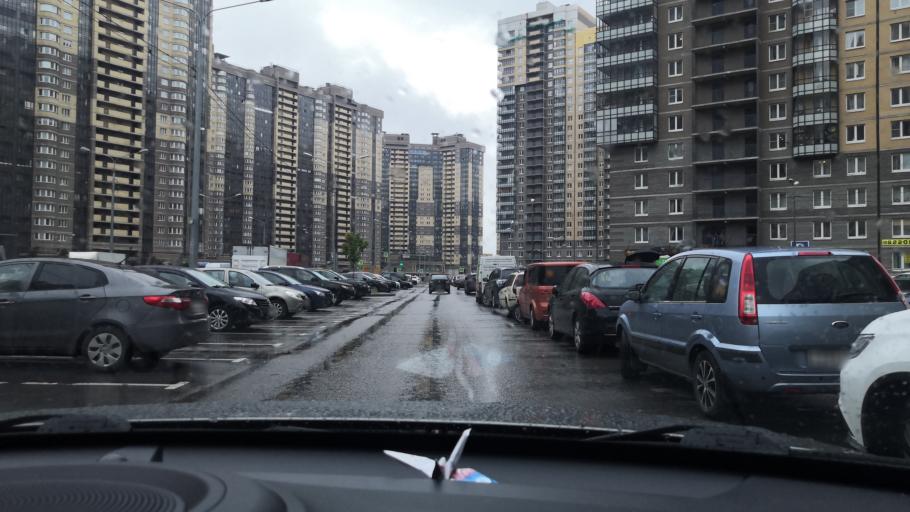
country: RU
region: Leningrad
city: Parnas
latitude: 60.0808
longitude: 30.3421
